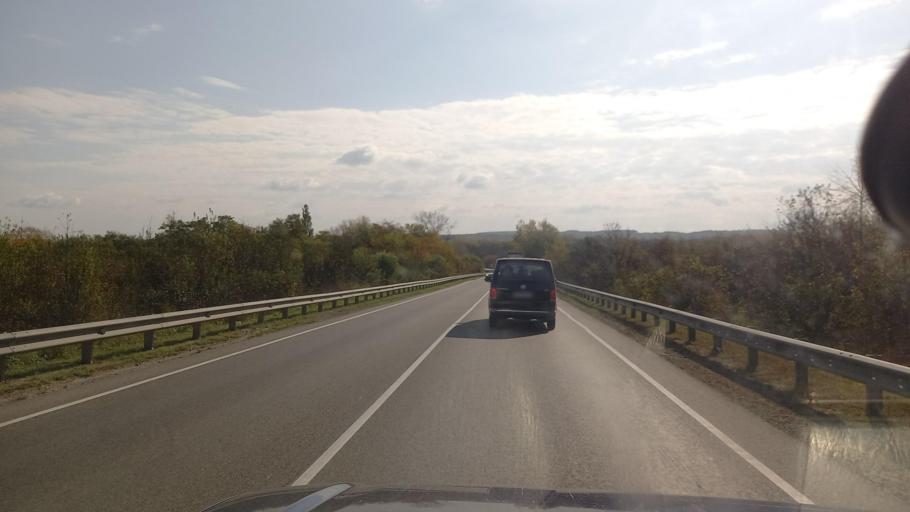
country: RU
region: Krasnodarskiy
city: Abinsk
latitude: 44.8465
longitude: 38.1491
